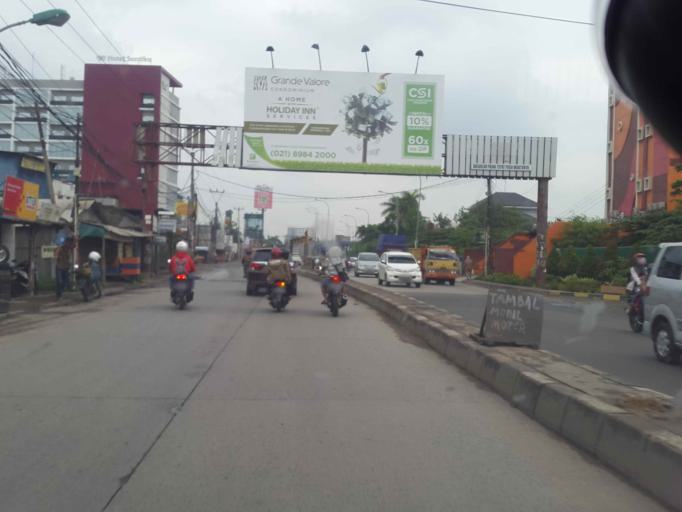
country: ID
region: West Java
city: Cikarang
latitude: -6.3084
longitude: 107.1439
